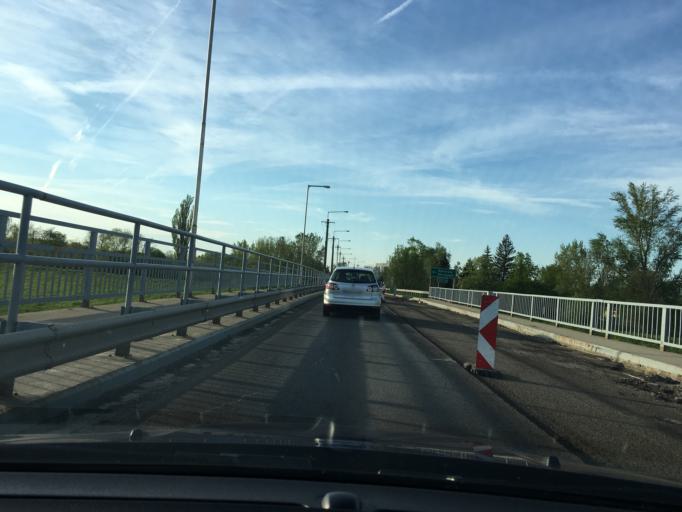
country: HU
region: Hajdu-Bihar
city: Berettyoujfalu
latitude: 47.2074
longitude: 21.5386
